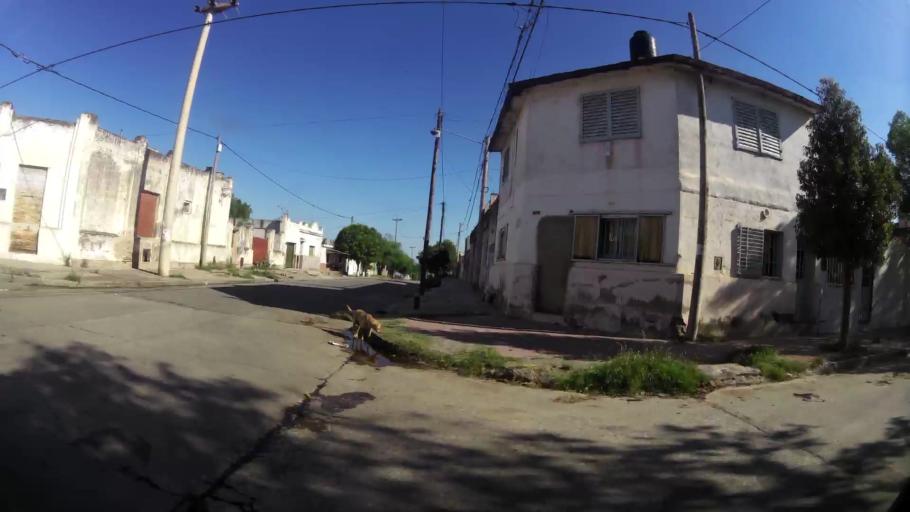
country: AR
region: Cordoba
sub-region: Departamento de Capital
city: Cordoba
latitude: -31.3985
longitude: -64.1547
